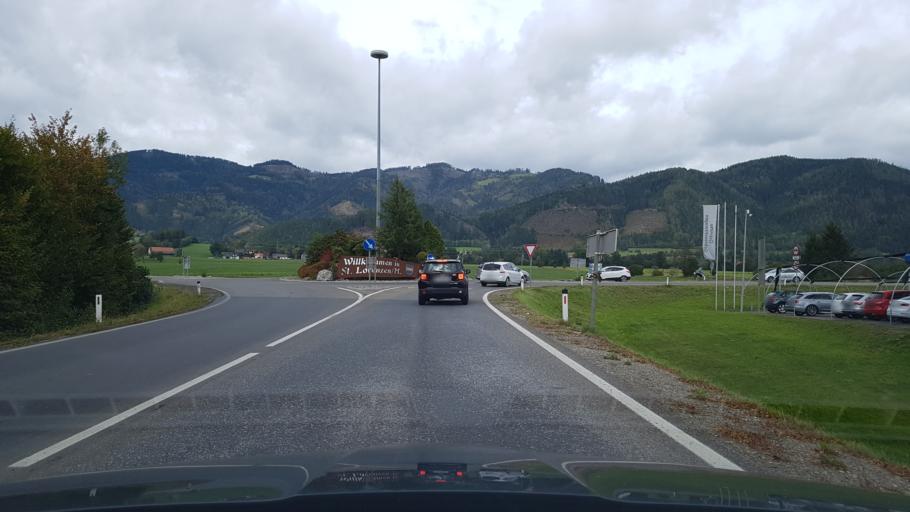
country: AT
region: Styria
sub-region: Politischer Bezirk Bruck-Muerzzuschlag
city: Sankt Marein im Muerztal
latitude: 47.4695
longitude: 15.3510
